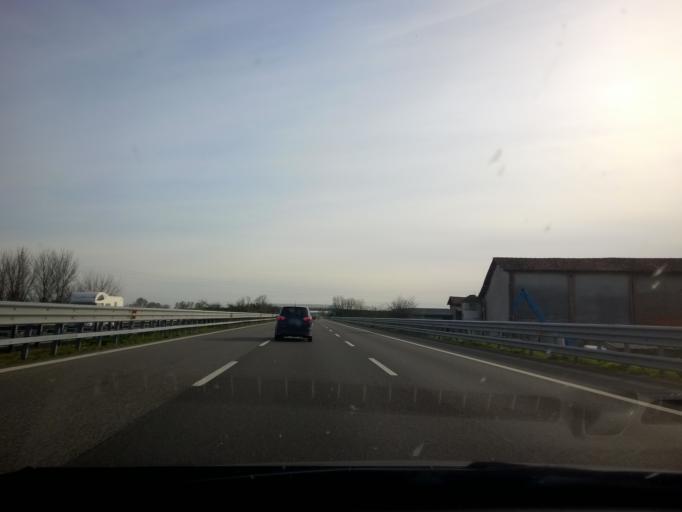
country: IT
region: Lombardy
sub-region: Provincia di Brescia
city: Bagnolo Mella
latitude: 45.4249
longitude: 10.1998
